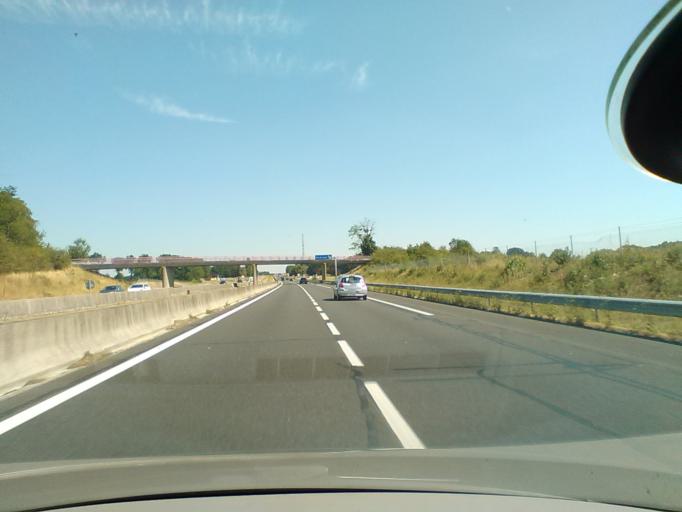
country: FR
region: Ile-de-France
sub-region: Departement de Seine-et-Marne
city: Egreville
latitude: 48.1627
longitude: 2.8755
